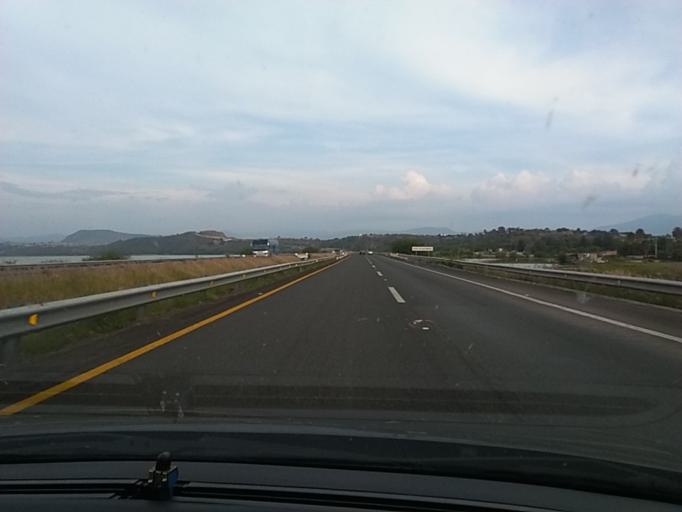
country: MX
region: Michoacan
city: Querendaro
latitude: 19.8854
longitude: -100.9476
